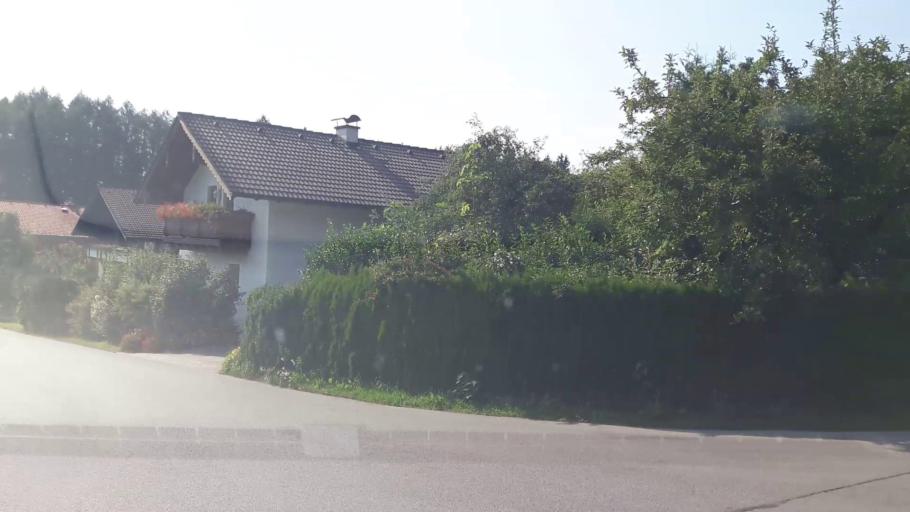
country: AT
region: Salzburg
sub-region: Politischer Bezirk Salzburg-Umgebung
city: Henndorf am Wallersee
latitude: 47.8909
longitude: 13.2133
